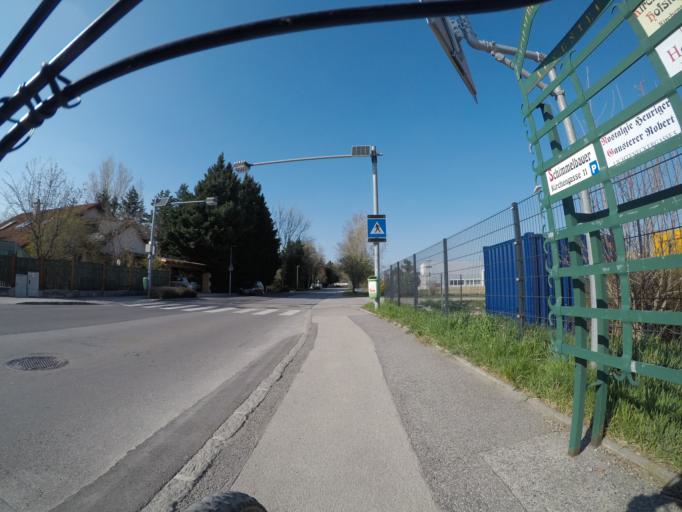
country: AT
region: Lower Austria
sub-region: Politischer Bezirk Modling
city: Neu-Guntramsdorf
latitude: 48.0586
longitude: 16.3237
